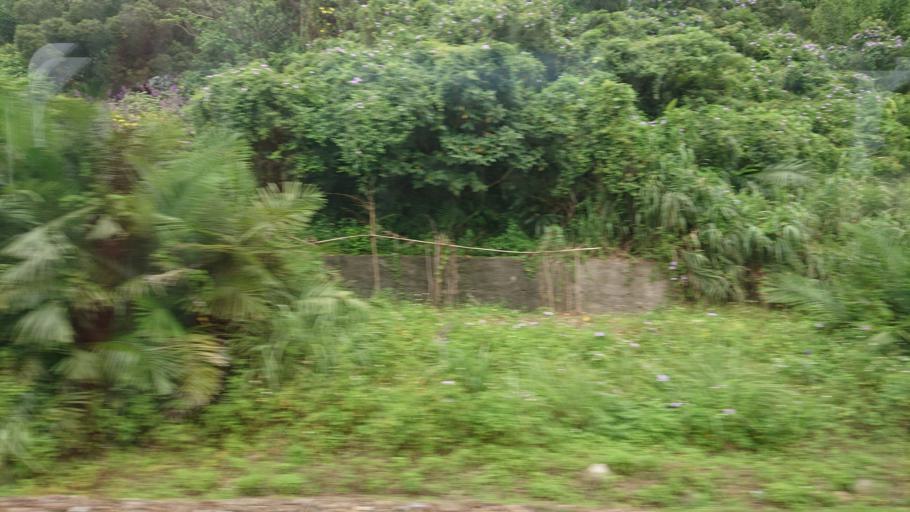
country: TW
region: Taiwan
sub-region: Keelung
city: Keelung
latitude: 24.9588
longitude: 121.9179
